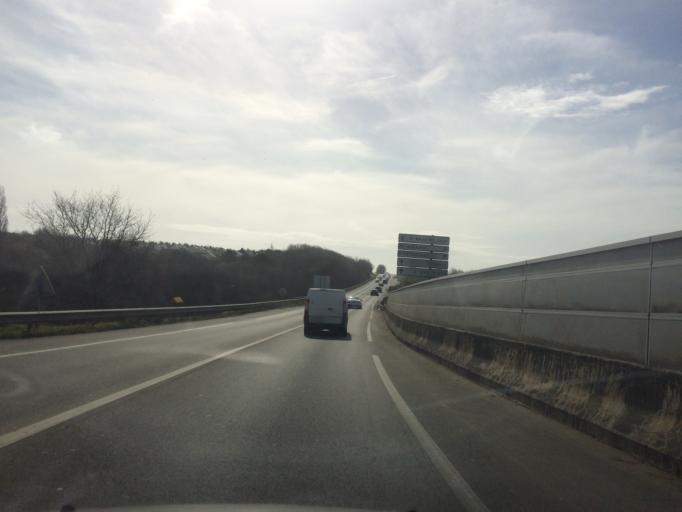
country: FR
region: Pays de la Loire
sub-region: Departement de la Loire-Atlantique
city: Saint-Nazaire
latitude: 47.2850
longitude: -2.2497
